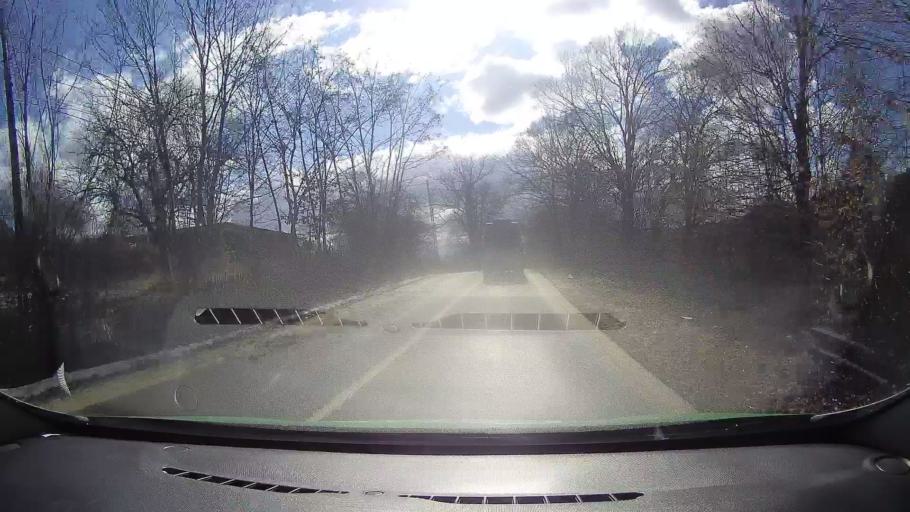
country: RO
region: Dambovita
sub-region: Comuna Runcu
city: Badeni
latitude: 45.1395
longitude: 25.4023
